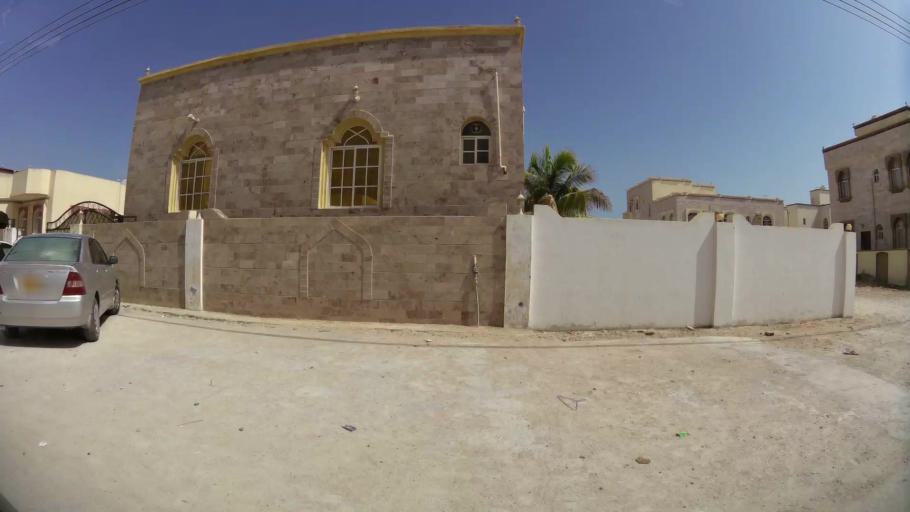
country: OM
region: Zufar
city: Salalah
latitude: 17.0487
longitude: 54.1564
